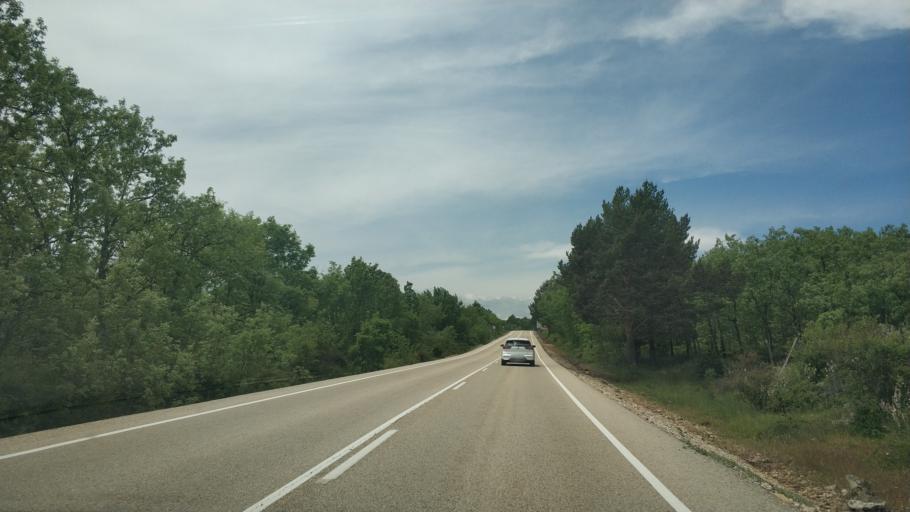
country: ES
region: Castille and Leon
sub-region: Provincia de Soria
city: Vinuesa
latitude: 41.8818
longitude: -2.7075
